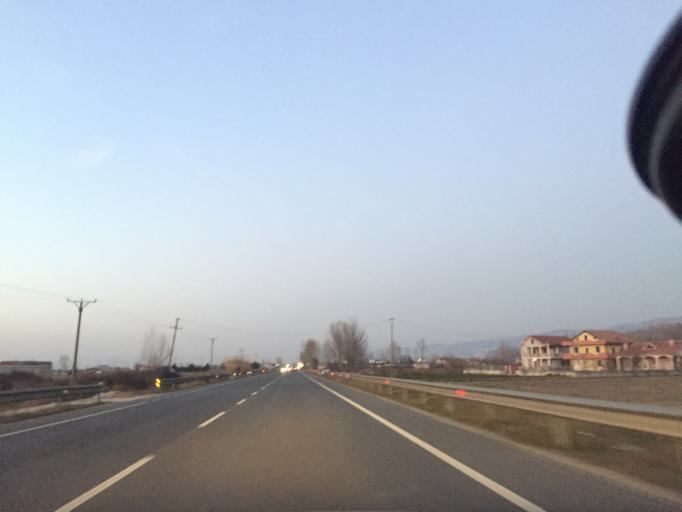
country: AL
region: Tirane
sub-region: Rrethi i Tiranes
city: Preze
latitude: 41.4513
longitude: 19.6889
